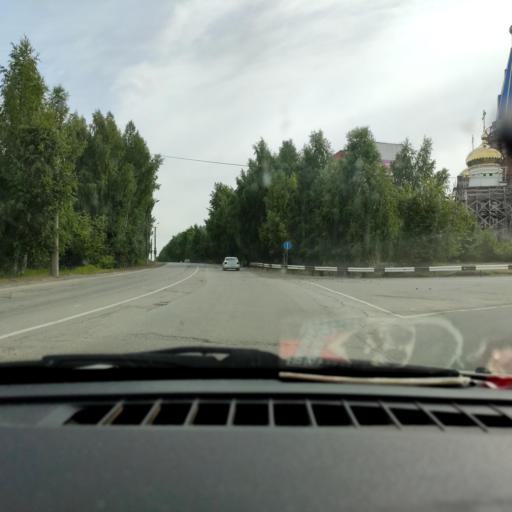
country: RU
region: Perm
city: Chusovoy
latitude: 58.2798
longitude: 57.8131
